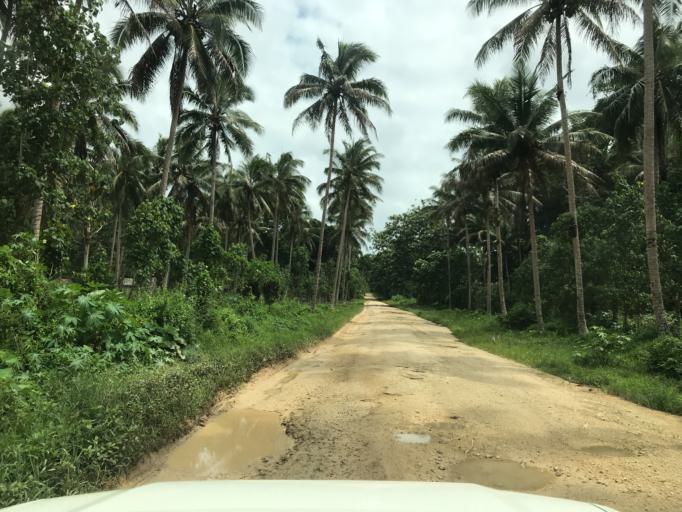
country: VU
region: Sanma
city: Port-Olry
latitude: -15.1766
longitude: 167.0932
